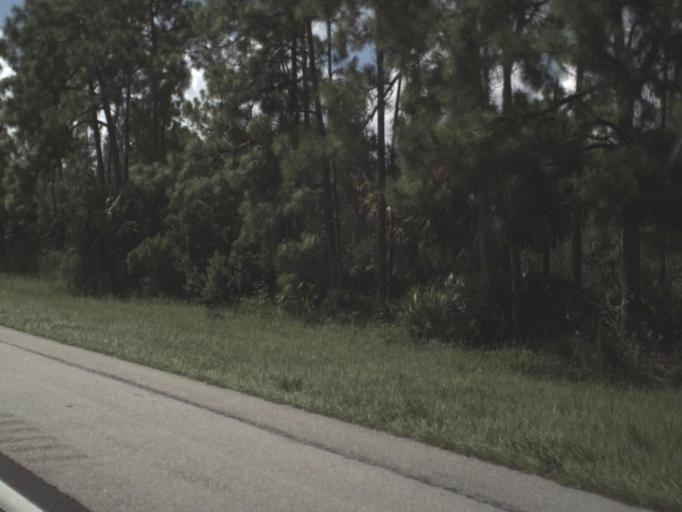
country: US
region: Florida
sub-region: Lee County
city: Three Oaks
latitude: 26.4569
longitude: -81.7867
